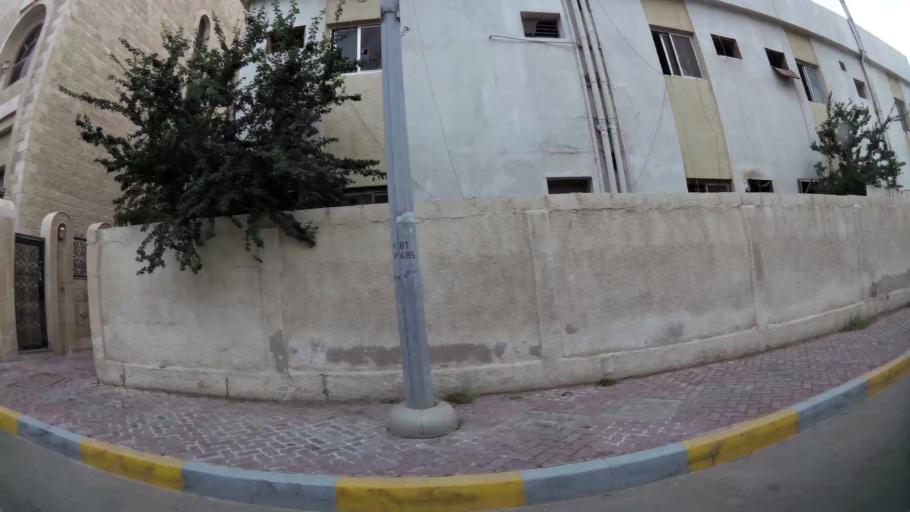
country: AE
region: Abu Dhabi
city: Abu Dhabi
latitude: 24.4469
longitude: 54.3987
